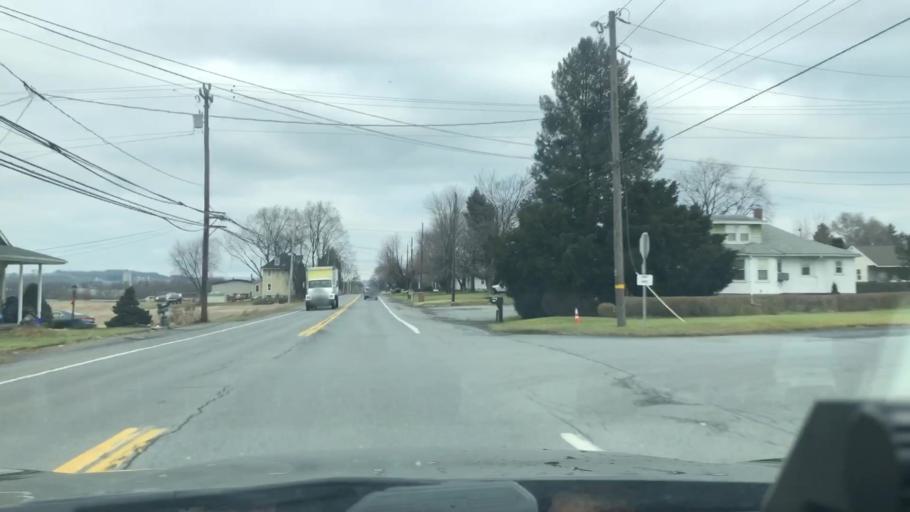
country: US
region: Pennsylvania
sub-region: Northampton County
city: Nazareth
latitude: 40.7088
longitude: -75.3267
